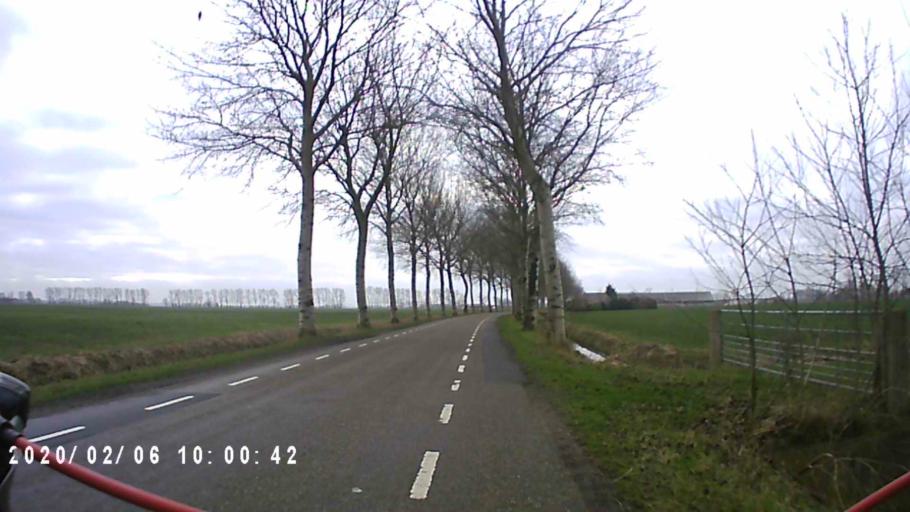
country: NL
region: Groningen
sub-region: Gemeente Zuidhorn
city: Aduard
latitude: 53.2651
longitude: 6.4906
